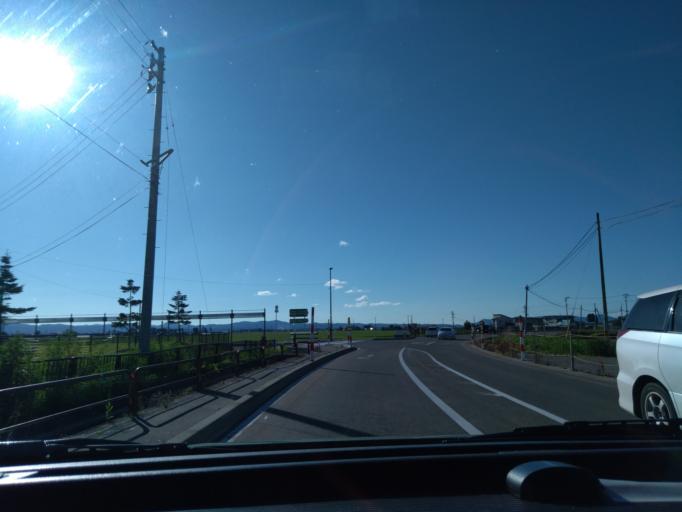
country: JP
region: Akita
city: Yokotemachi
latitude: 39.3300
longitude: 140.5460
